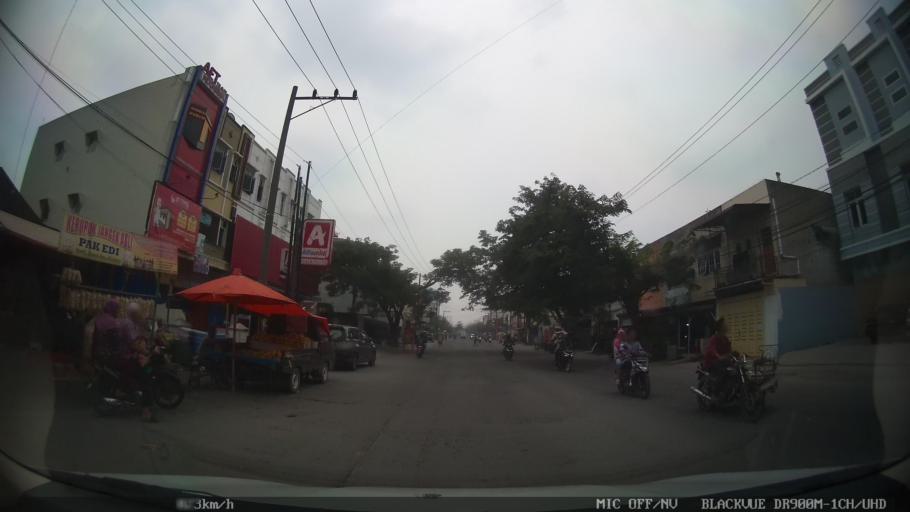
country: ID
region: North Sumatra
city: Medan
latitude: 3.5818
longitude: 98.7126
